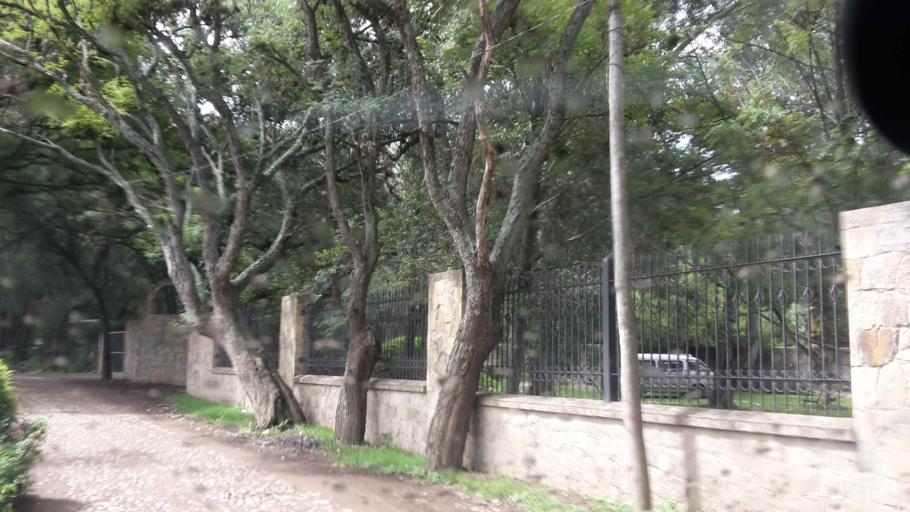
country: BO
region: Cochabamba
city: Cochabamba
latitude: -17.3602
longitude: -66.2156
